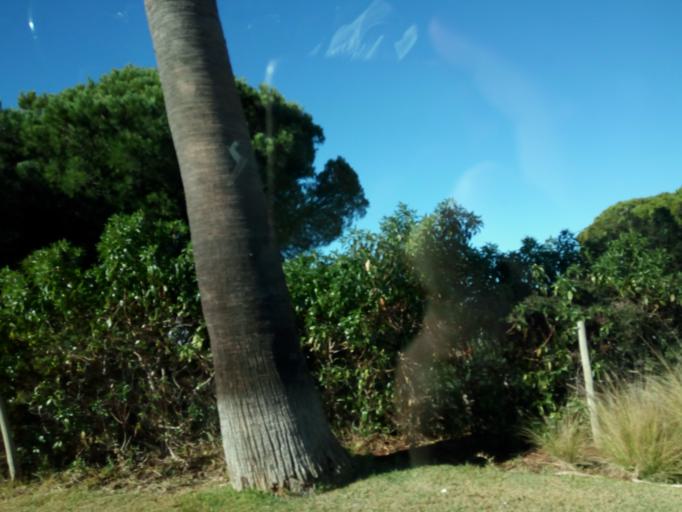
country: PT
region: Faro
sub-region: Loule
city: Vilamoura
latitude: 37.1139
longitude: -8.1185
